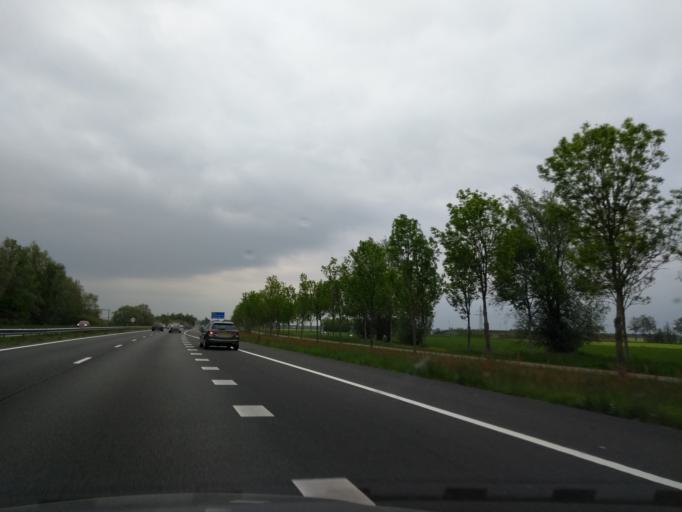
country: NL
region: Drenthe
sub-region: Gemeente Meppel
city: Meppel
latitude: 52.7077
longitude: 6.2060
